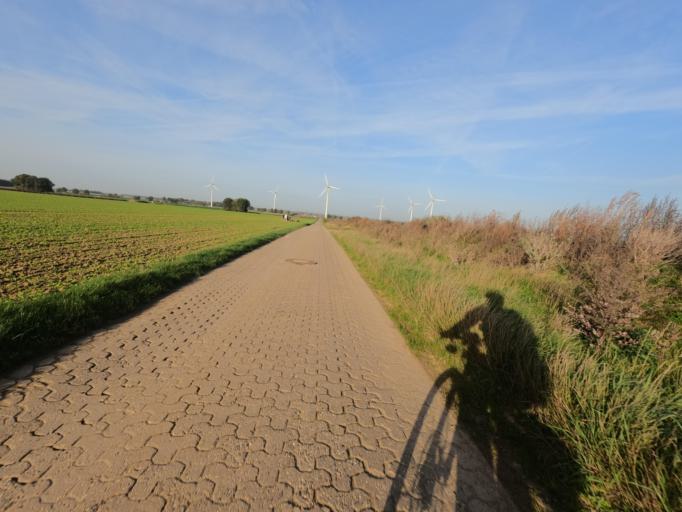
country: DE
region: North Rhine-Westphalia
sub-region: Regierungsbezirk Koln
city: Titz
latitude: 51.0615
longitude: 6.4213
